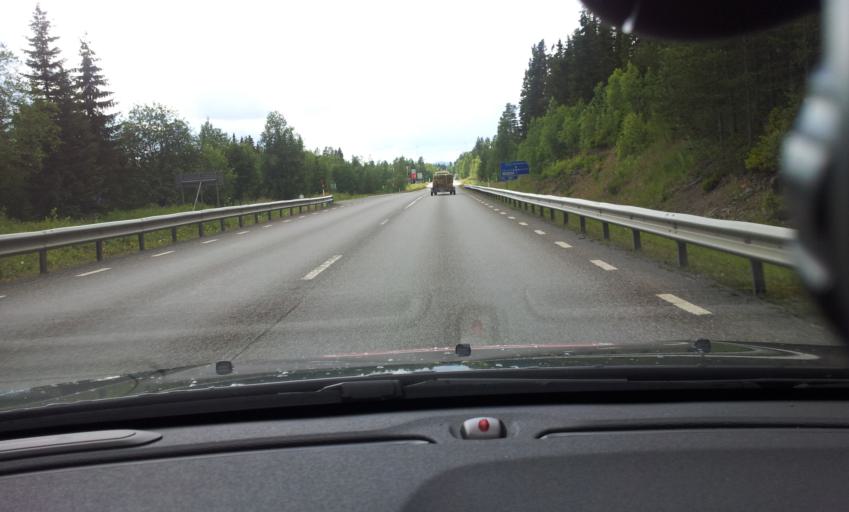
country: SE
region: Jaemtland
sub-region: Are Kommun
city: Jarpen
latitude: 63.3112
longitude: 13.6935
